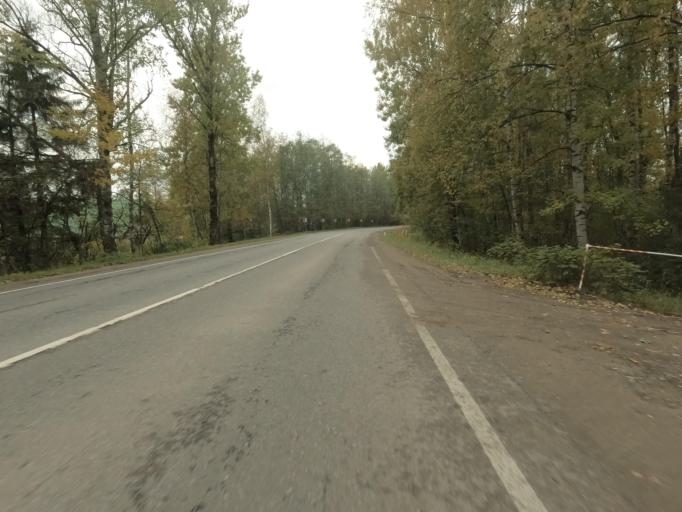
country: RU
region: Leningrad
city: Pavlovo
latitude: 59.7880
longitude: 30.9637
